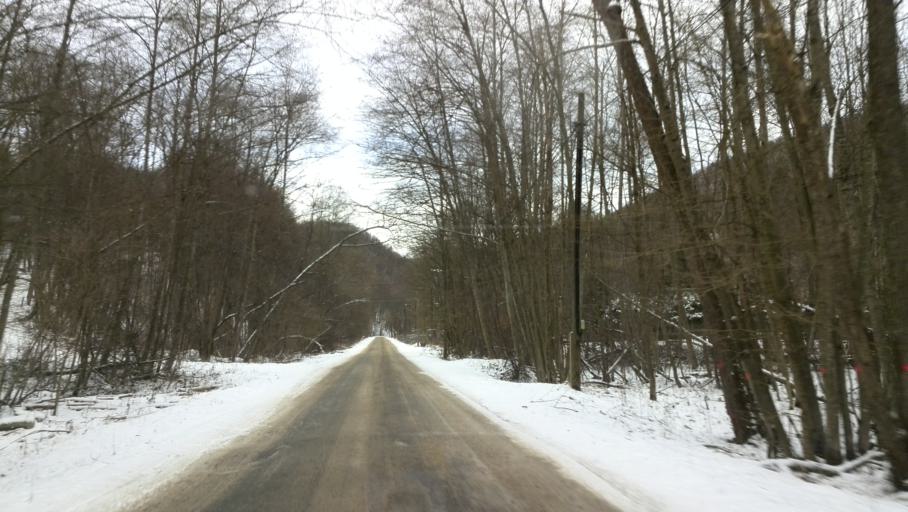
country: SK
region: Kosicky
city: Gelnica
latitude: 48.8146
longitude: 21.0608
